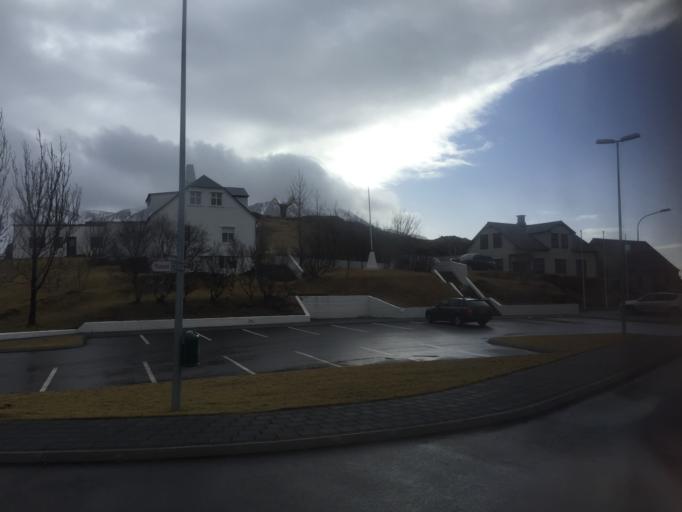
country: IS
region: West
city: Borgarnes
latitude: 64.5365
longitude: -21.9229
